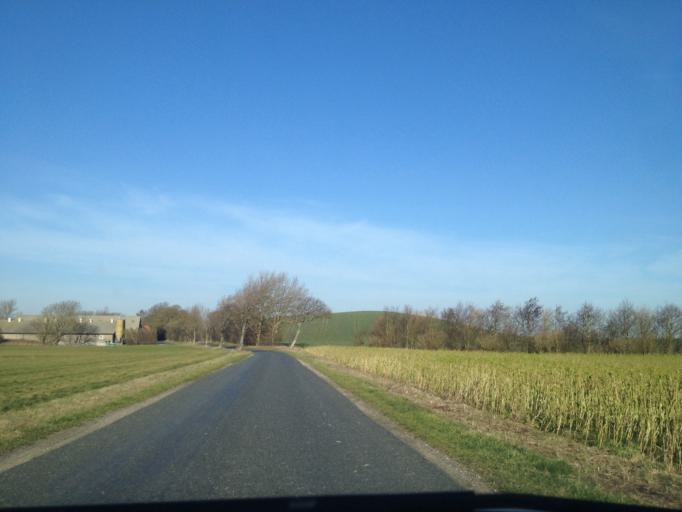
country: DK
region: South Denmark
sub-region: Kerteminde Kommune
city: Munkebo
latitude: 55.5577
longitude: 10.6145
